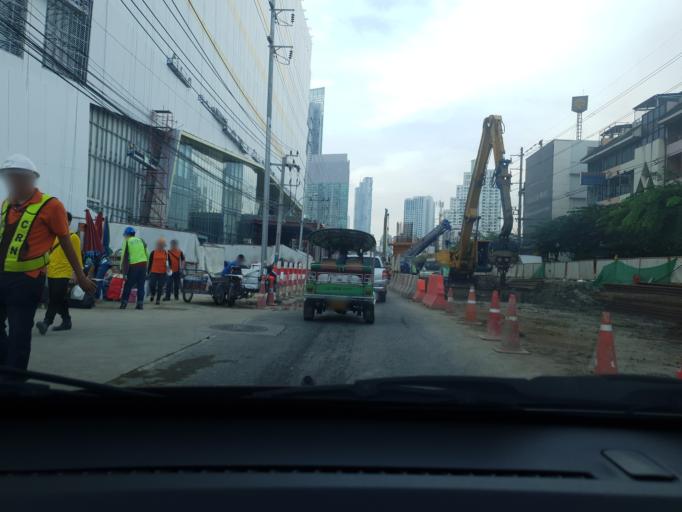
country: TH
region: Bangkok
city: Khlong San
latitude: 13.7276
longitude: 100.5090
